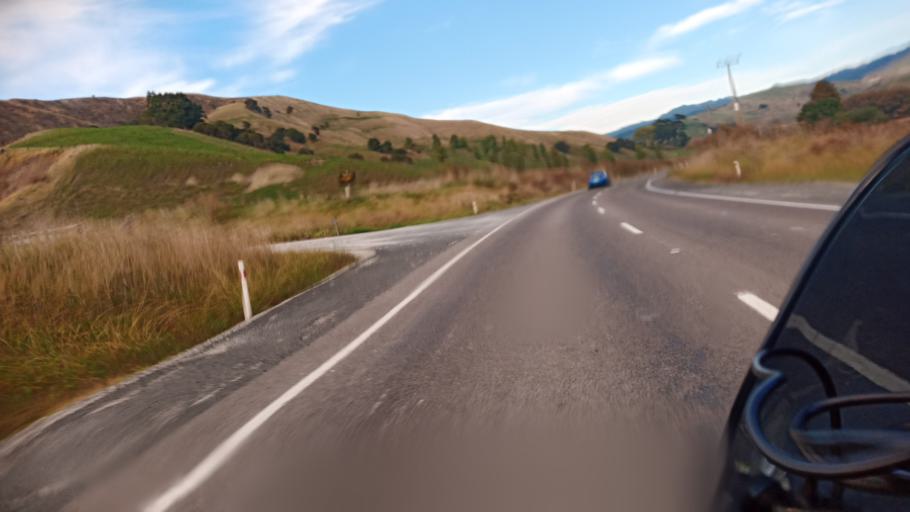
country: NZ
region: Gisborne
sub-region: Gisborne District
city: Gisborne
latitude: -38.7914
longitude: 177.9143
